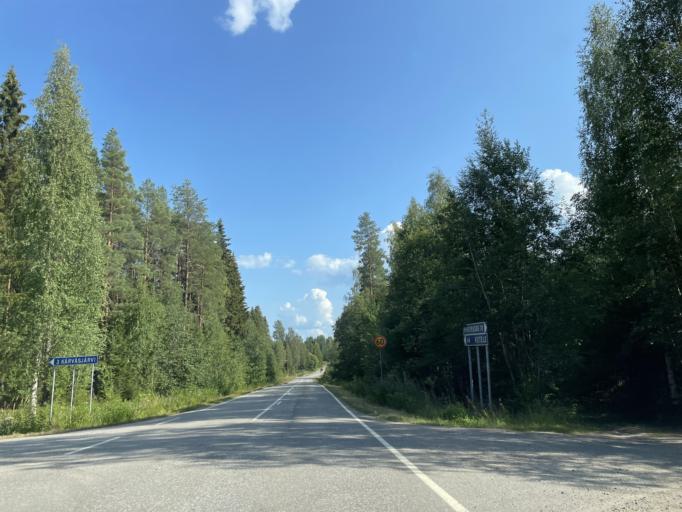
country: FI
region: Central Finland
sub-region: Saarijaervi-Viitasaari
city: Pihtipudas
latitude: 63.3630
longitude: 25.7419
